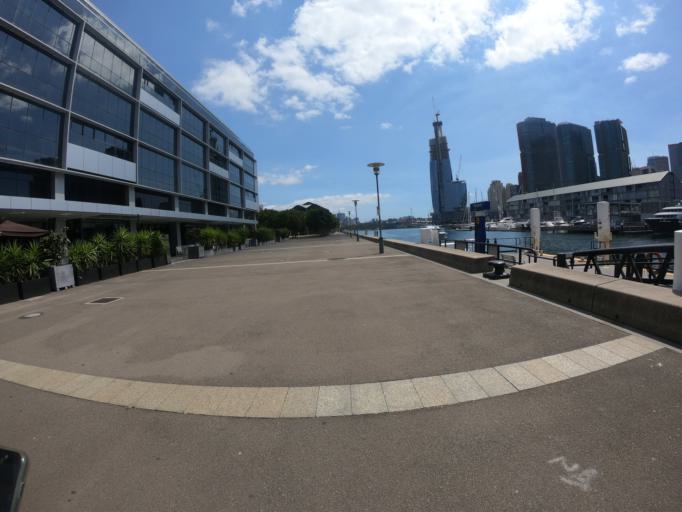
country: AU
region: New South Wales
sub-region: Leichhardt
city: Balmain East
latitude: -33.8670
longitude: 151.1962
